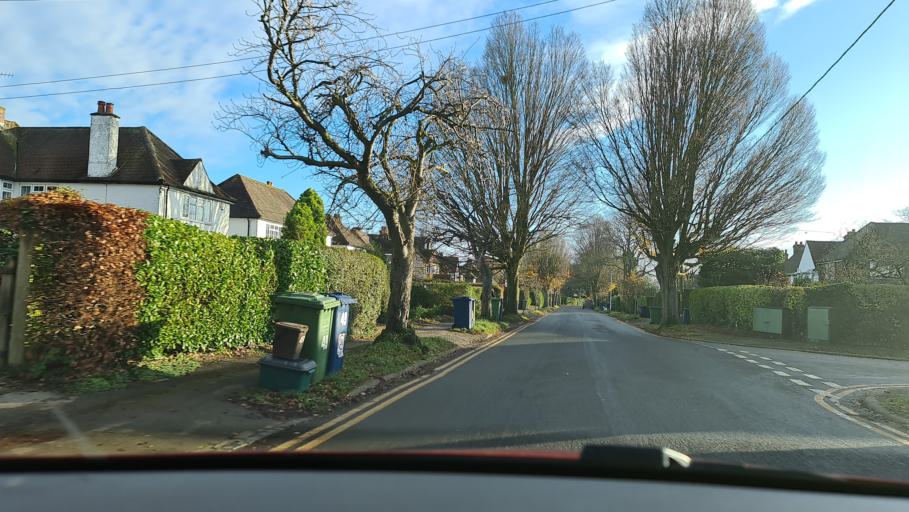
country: GB
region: England
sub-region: Buckinghamshire
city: Amersham on the Hill
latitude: 51.6723
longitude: -0.6010
